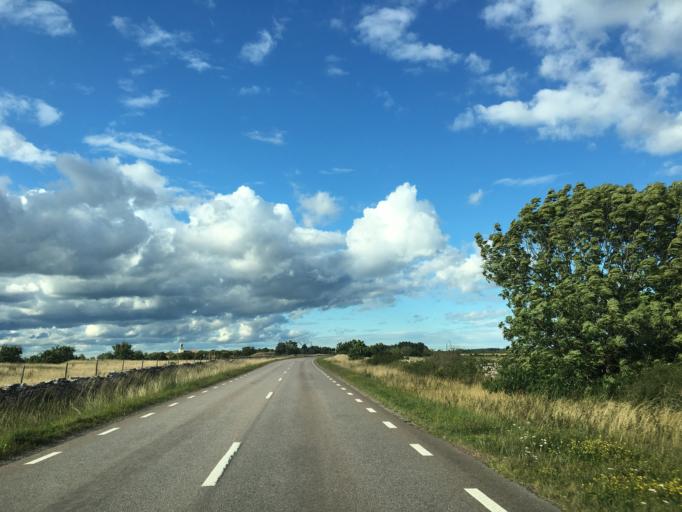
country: SE
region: Kalmar
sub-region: Morbylanga Kommun
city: Moerbylanga
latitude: 56.5316
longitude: 16.4428
